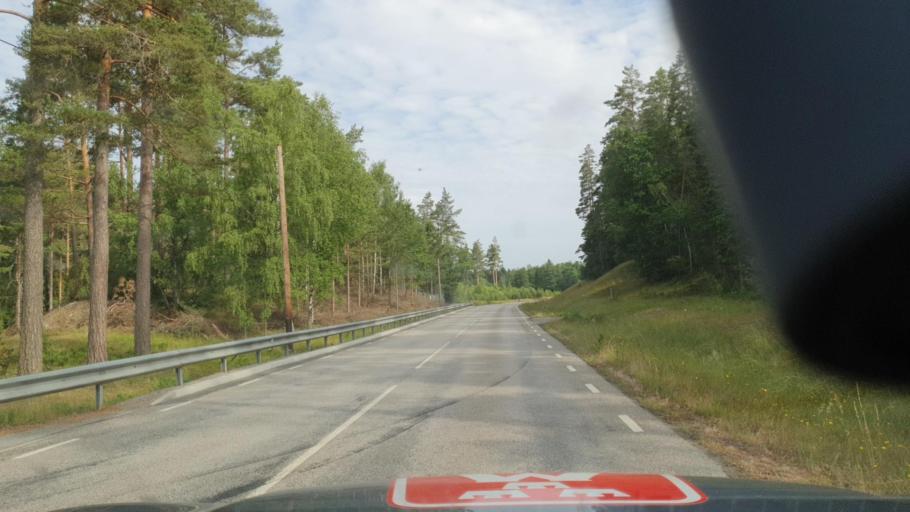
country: SE
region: Kalmar
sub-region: Nybro Kommun
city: Nybro
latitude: 56.7091
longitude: 15.9698
